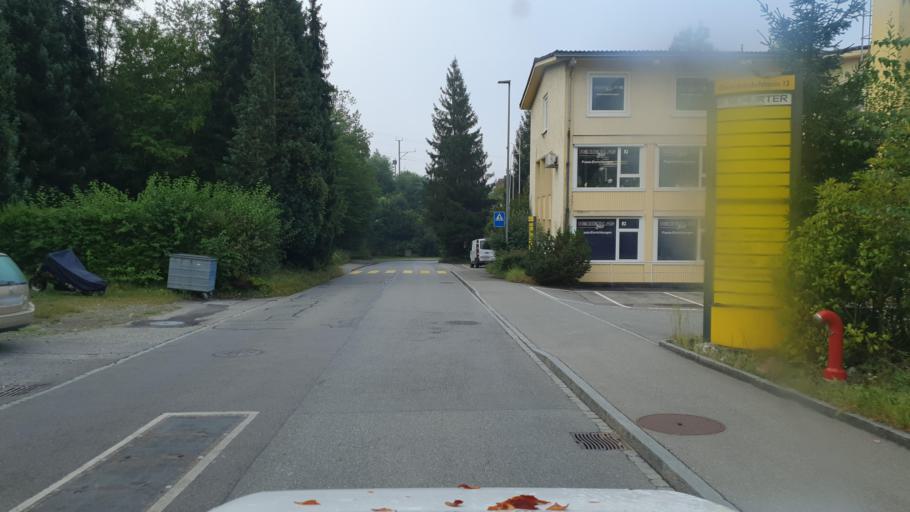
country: CH
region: Aargau
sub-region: Bezirk Baden
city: Mellingen
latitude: 47.4291
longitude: 8.2727
